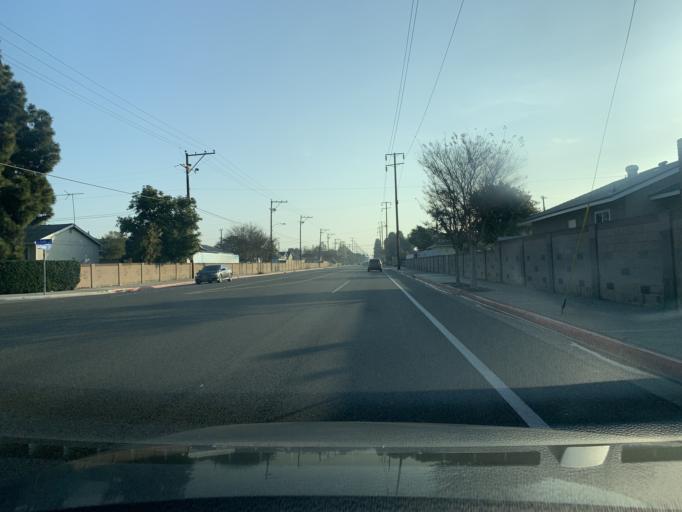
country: US
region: California
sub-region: Orange County
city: Westminster
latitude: 33.7372
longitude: -118.0196
